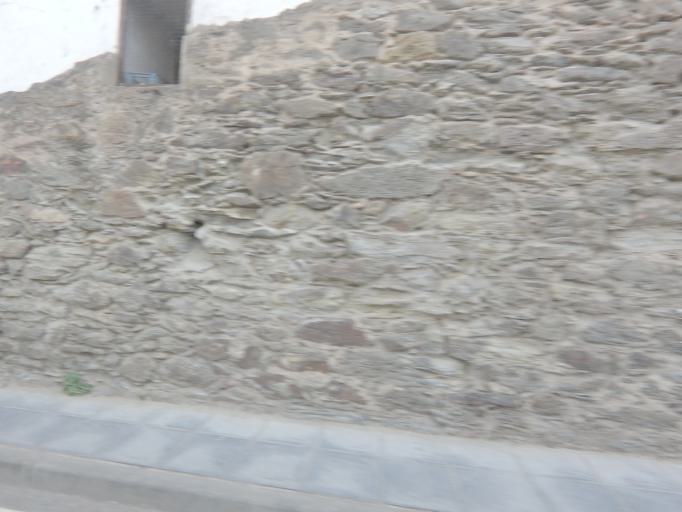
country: ES
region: Extremadura
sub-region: Provincia de Caceres
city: Coria
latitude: 39.9837
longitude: -6.5340
